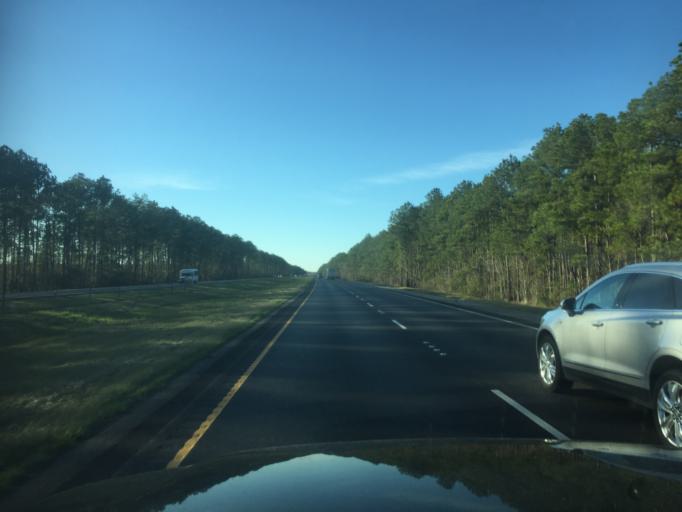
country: US
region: Louisiana
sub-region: Saint Tammany Parish
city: Lacombe
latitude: 30.3771
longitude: -89.9675
